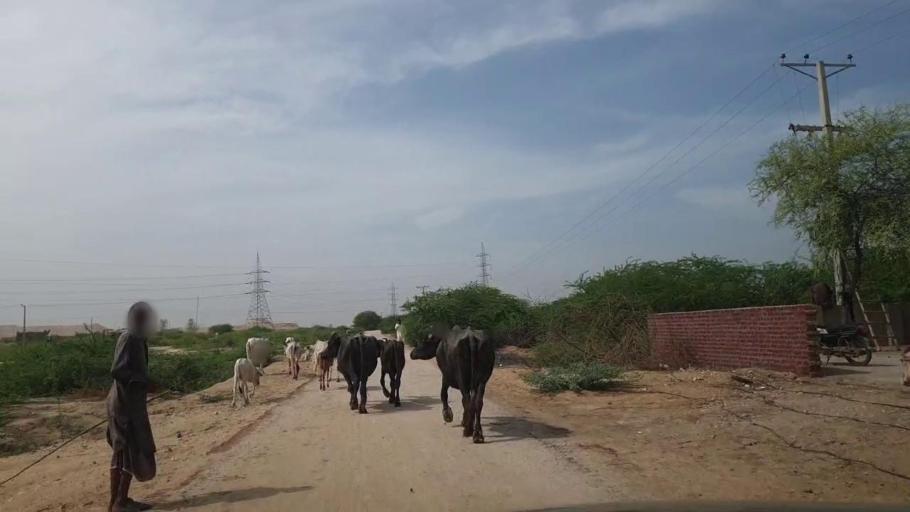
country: PK
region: Sindh
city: Kot Diji
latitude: 27.3636
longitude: 68.7635
